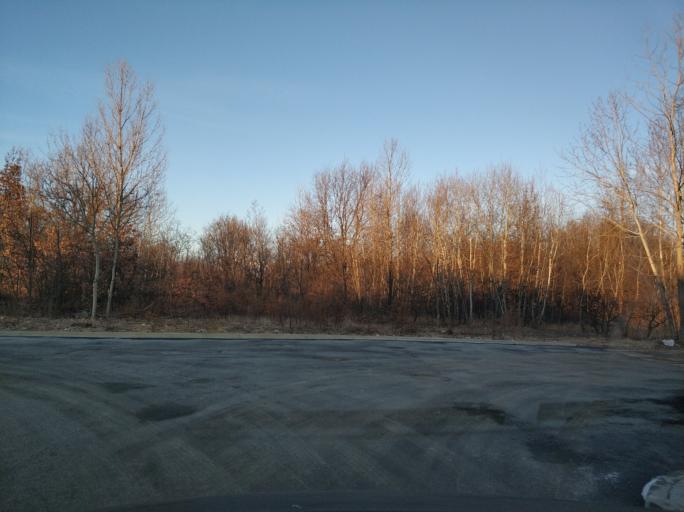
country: IT
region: Piedmont
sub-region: Provincia di Torino
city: Grosso
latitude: 45.2627
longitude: 7.5716
